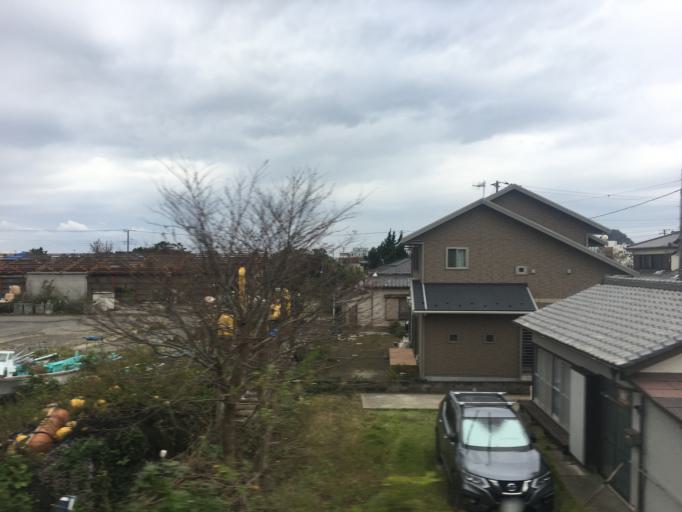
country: JP
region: Chiba
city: Tateyama
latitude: 35.0961
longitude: 139.8493
